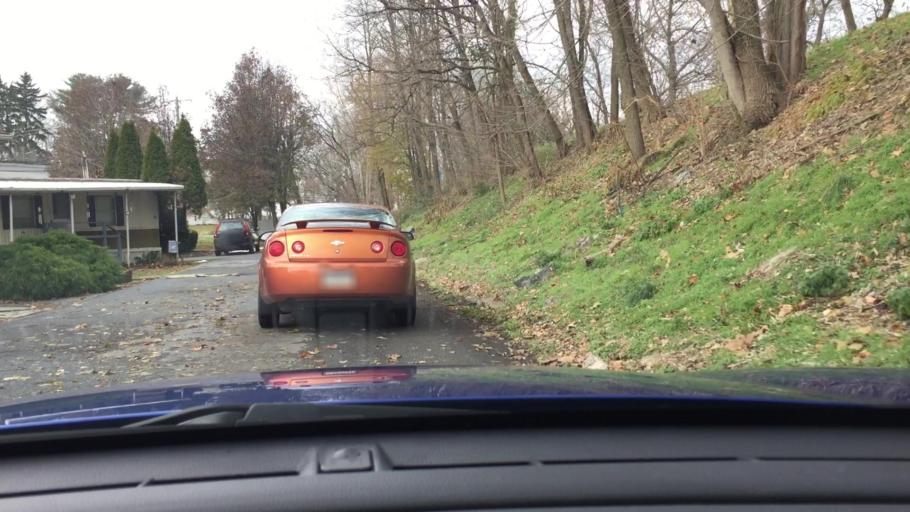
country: US
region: Pennsylvania
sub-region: Cumberland County
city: Shiremanstown
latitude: 40.2237
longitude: -76.9734
